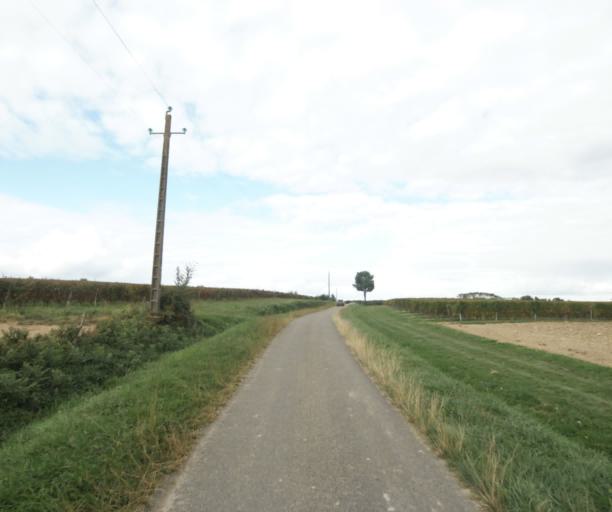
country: FR
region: Midi-Pyrenees
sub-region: Departement du Gers
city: Eauze
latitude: 43.9199
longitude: 0.1221
